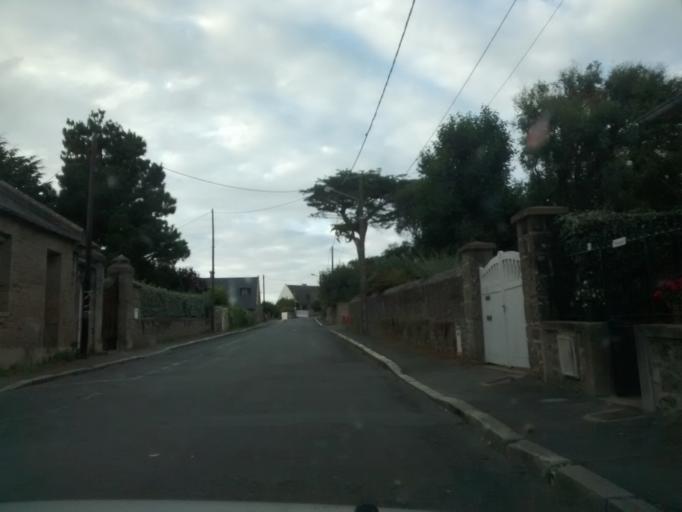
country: FR
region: Brittany
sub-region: Departement d'Ille-et-Vilaine
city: Saint-Lunaire
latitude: 48.6395
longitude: -2.1156
